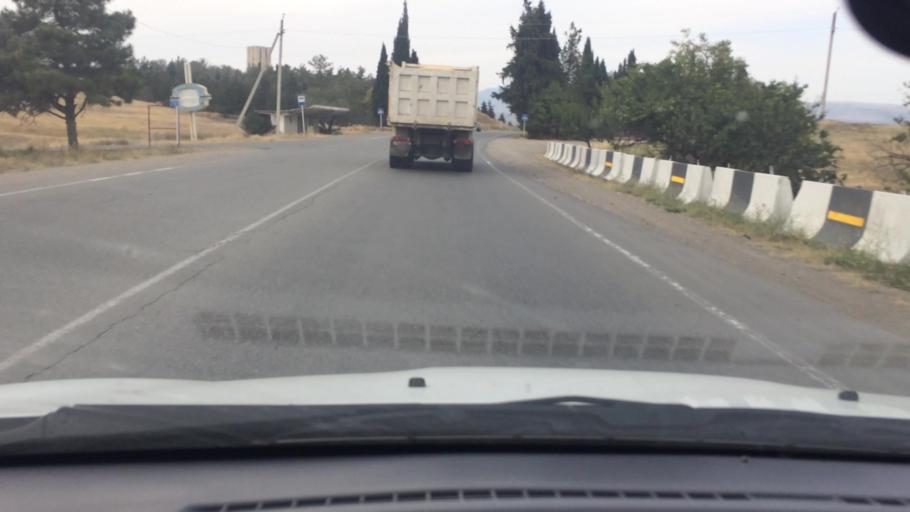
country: GE
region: Kvemo Kartli
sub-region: Marneuli
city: Marneuli
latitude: 41.5215
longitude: 44.7794
